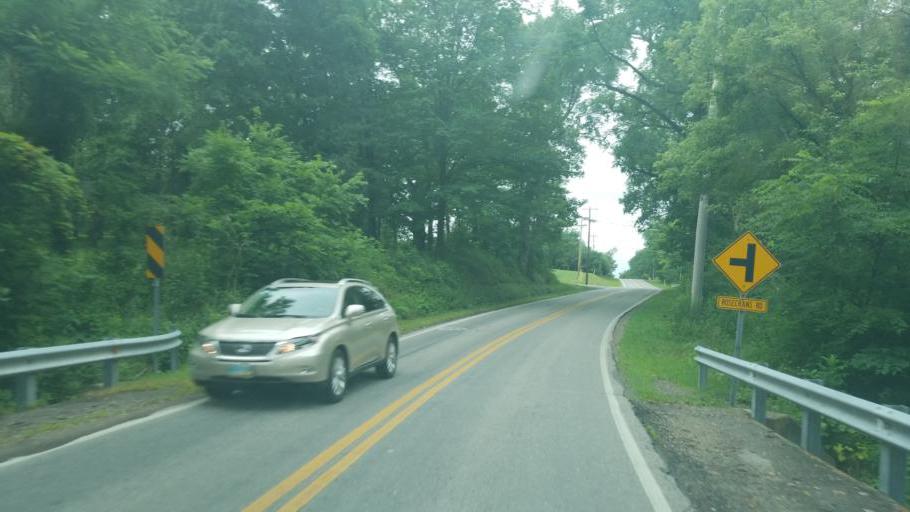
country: US
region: Ohio
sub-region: Delaware County
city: Sunbury
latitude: 40.2898
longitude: -82.8796
